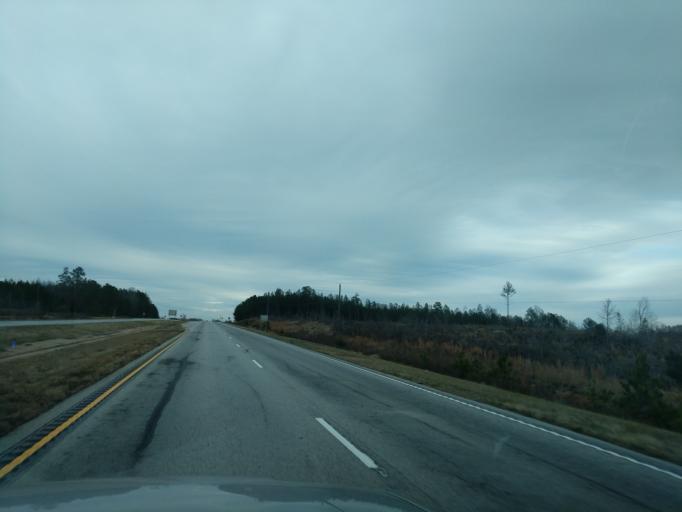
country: US
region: South Carolina
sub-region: Laurens County
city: Clinton
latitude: 34.3455
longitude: -81.9732
